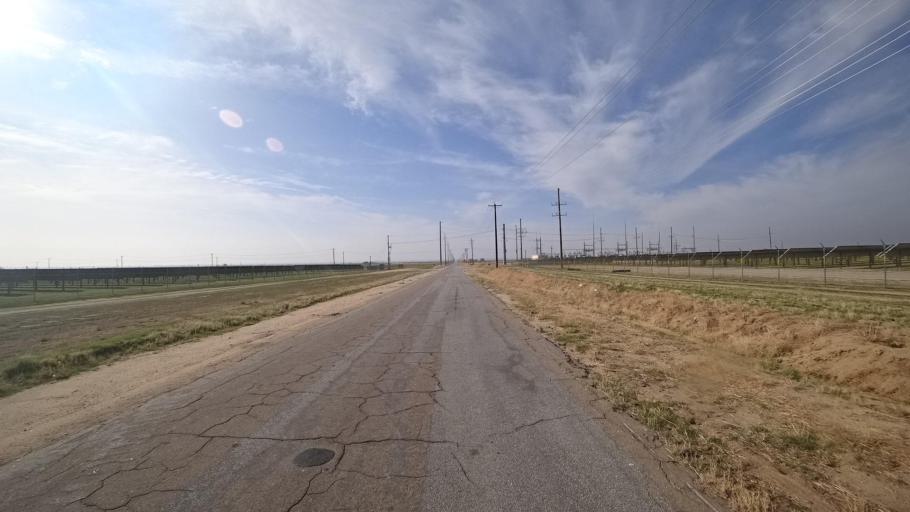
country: US
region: California
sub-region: Kern County
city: Lamont
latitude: 35.3258
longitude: -118.8222
